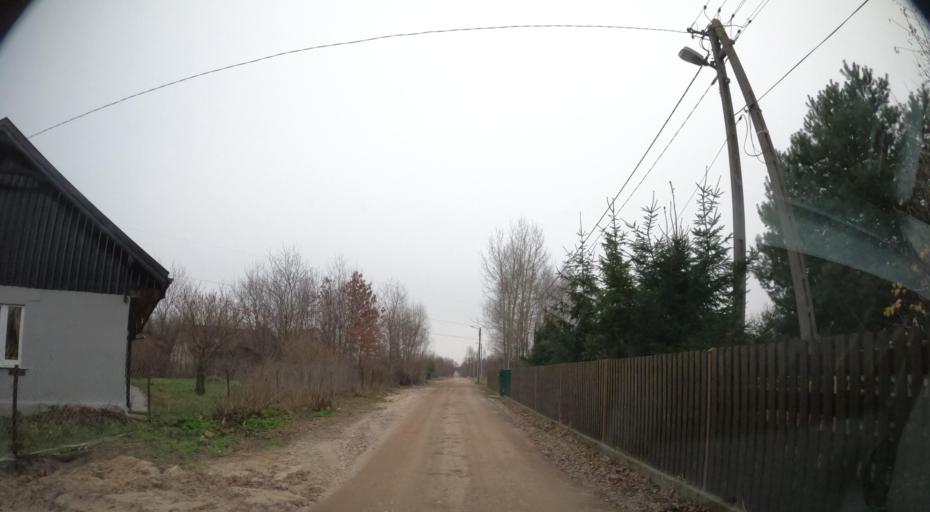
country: PL
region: Masovian Voivodeship
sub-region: Powiat radomski
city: Jastrzebia
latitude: 51.4868
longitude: 21.1889
